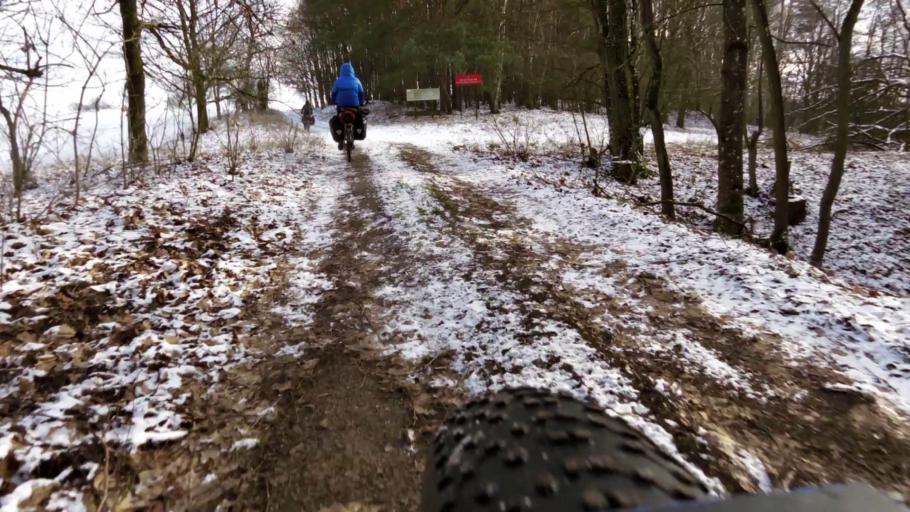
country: PL
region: West Pomeranian Voivodeship
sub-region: Powiat walecki
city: Tuczno
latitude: 53.3019
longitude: 16.2739
